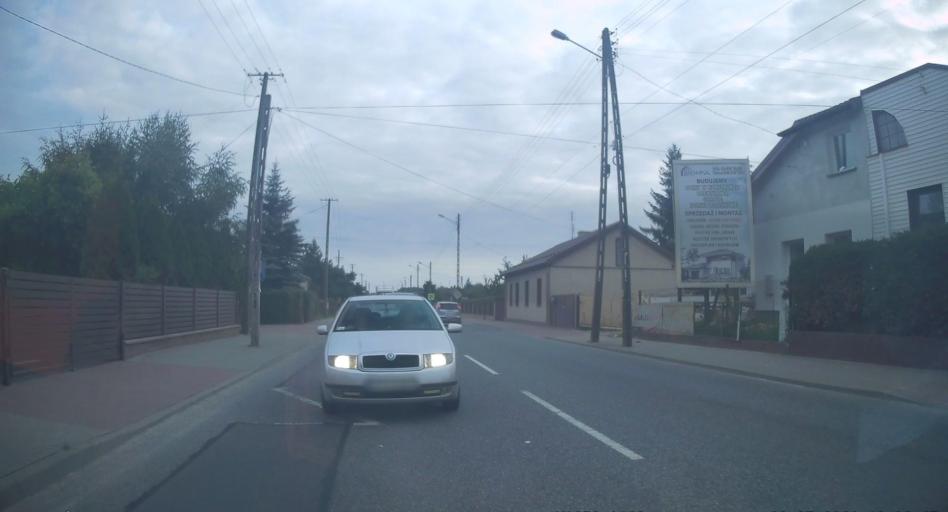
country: PL
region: Lodz Voivodeship
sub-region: Powiat radomszczanski
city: Kamiensk
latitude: 51.1975
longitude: 19.4993
